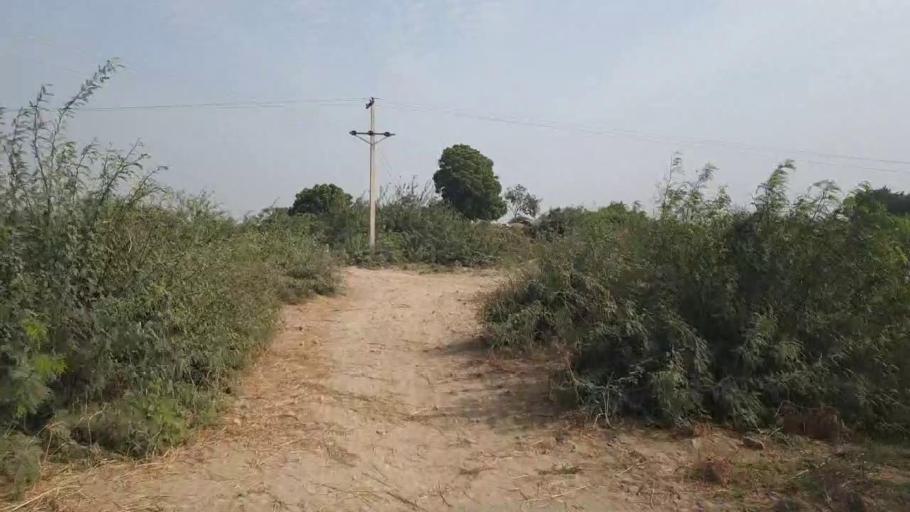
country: PK
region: Sindh
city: Tando Muhammad Khan
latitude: 25.1626
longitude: 68.4703
